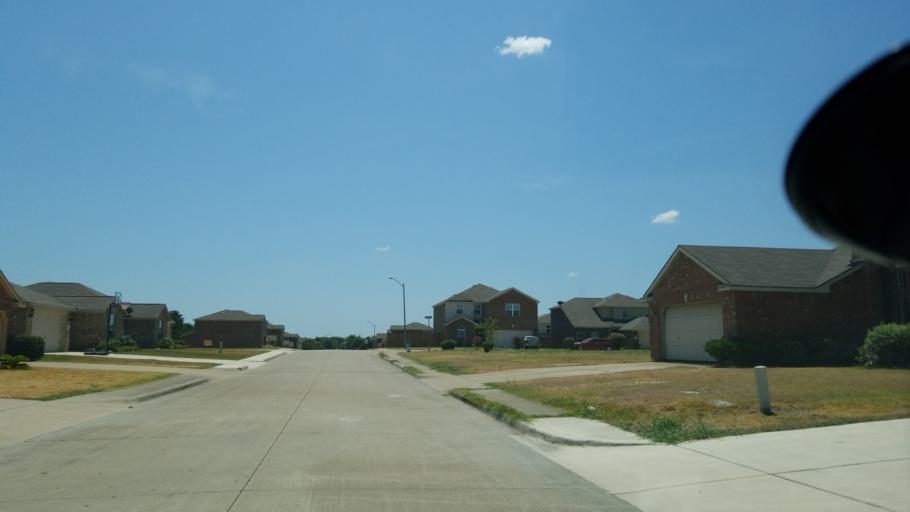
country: US
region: Texas
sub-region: Dallas County
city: Duncanville
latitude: 32.6435
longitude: -96.8841
